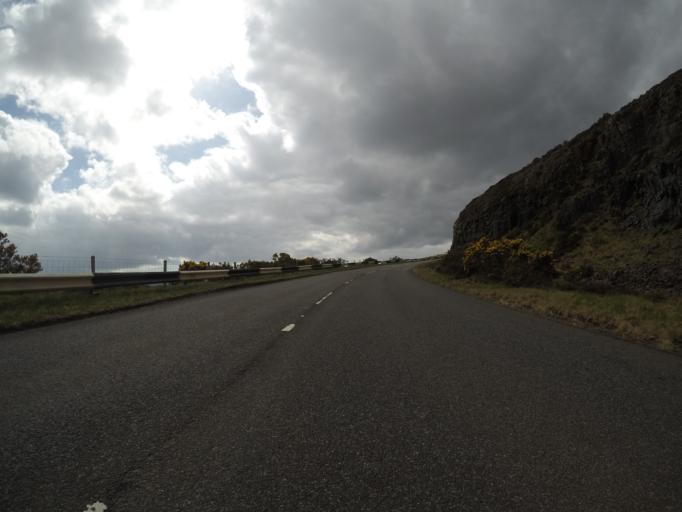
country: GB
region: Scotland
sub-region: Highland
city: Isle of Skye
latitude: 57.3052
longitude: -6.3108
